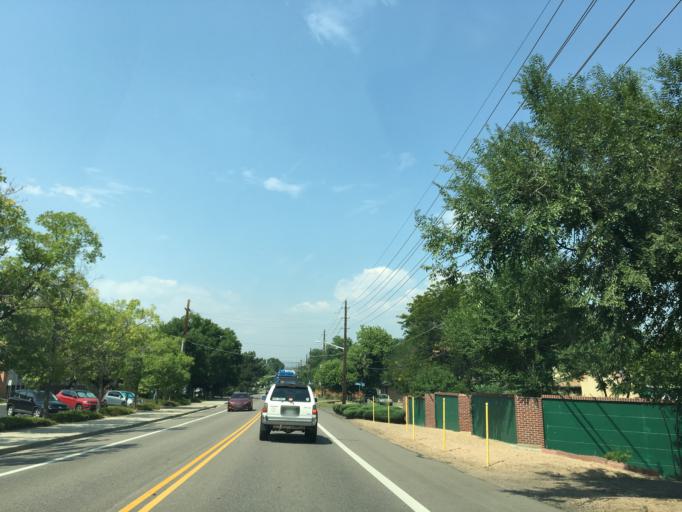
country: US
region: Colorado
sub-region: Jefferson County
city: Wheat Ridge
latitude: 39.7475
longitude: -105.1150
